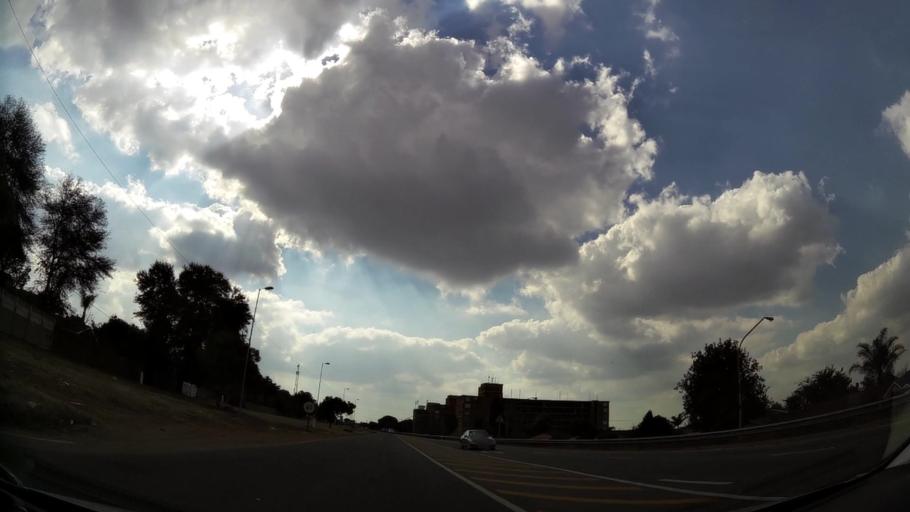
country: ZA
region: Gauteng
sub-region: City of Tshwane Metropolitan Municipality
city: Centurion
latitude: -25.8271
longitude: 28.2555
